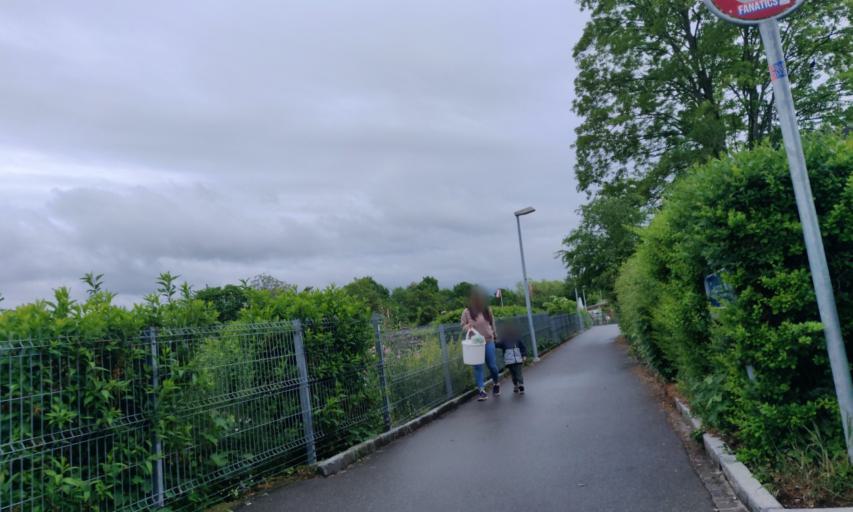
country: CH
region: Basel-Landschaft
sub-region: Bezirk Arlesheim
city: Birsfelden
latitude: 47.5689
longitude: 7.6309
